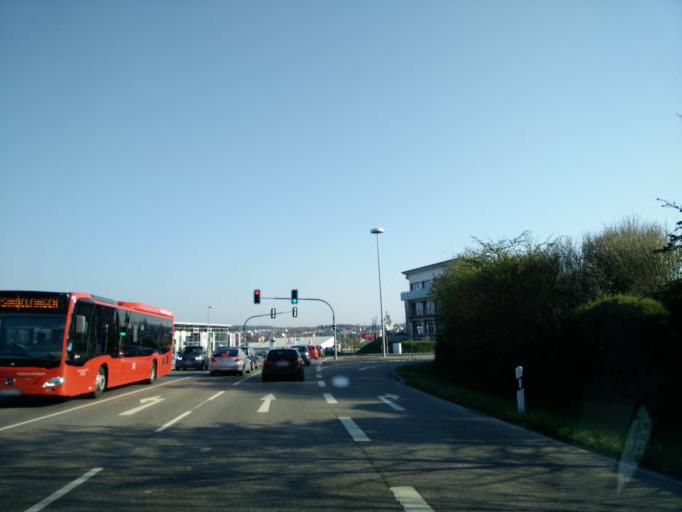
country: DE
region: Baden-Wuerttemberg
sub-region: Karlsruhe Region
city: Calw
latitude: 48.7028
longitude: 8.7600
